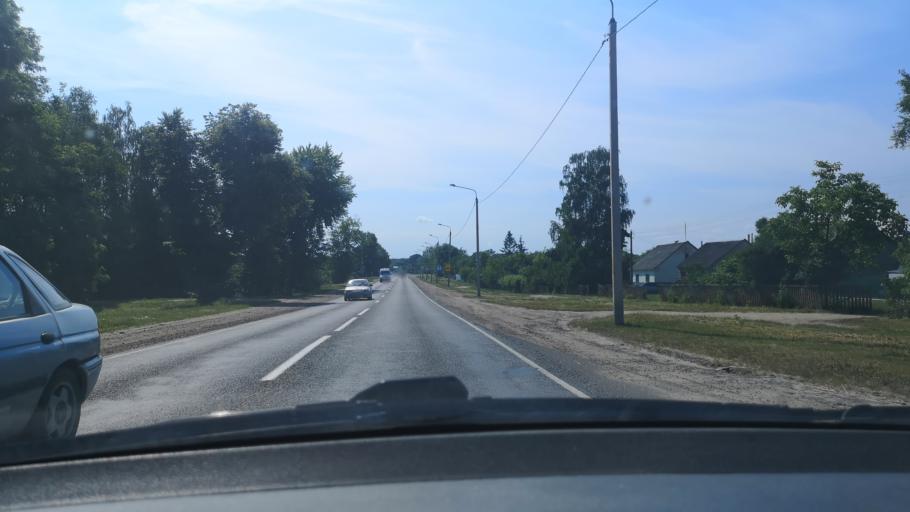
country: BY
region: Brest
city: Brest
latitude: 52.1600
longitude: 23.6674
